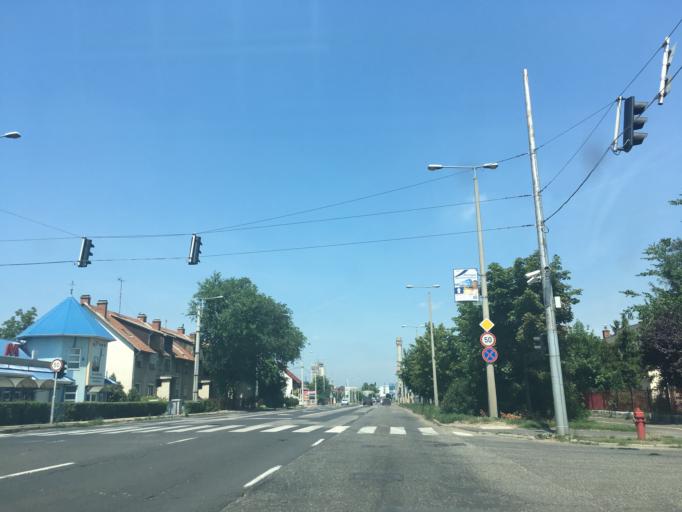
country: HU
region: Hajdu-Bihar
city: Debrecen
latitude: 47.5110
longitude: 21.6299
